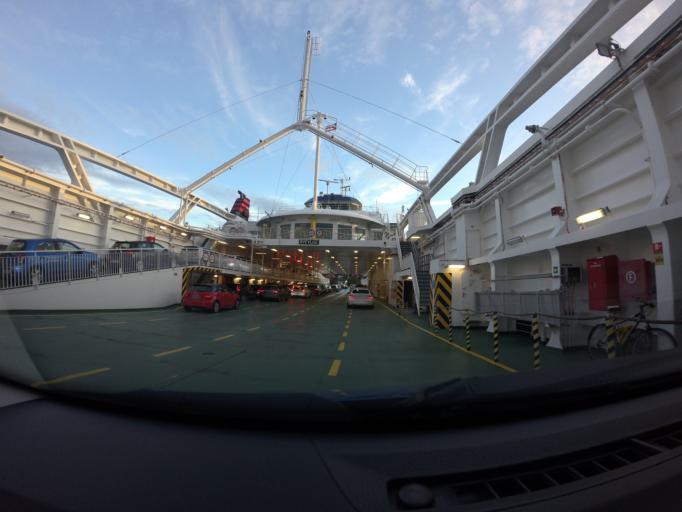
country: NO
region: Rogaland
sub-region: Stavanger
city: Stavanger
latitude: 58.9730
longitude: 5.7407
